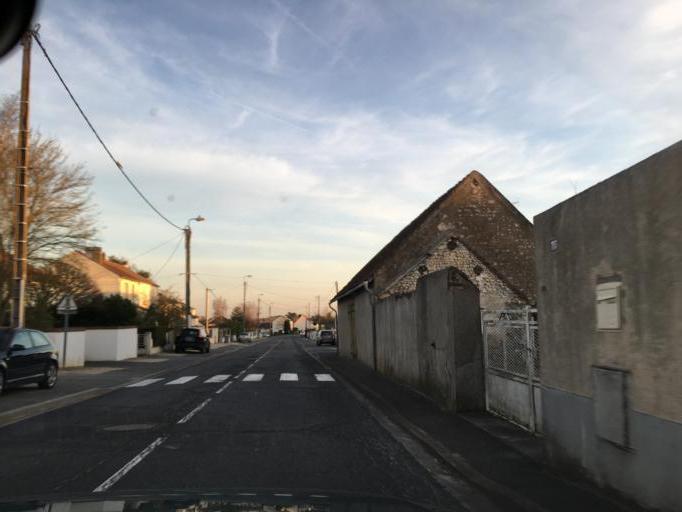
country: FR
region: Centre
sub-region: Departement du Loiret
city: Saran
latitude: 47.9415
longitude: 1.8708
